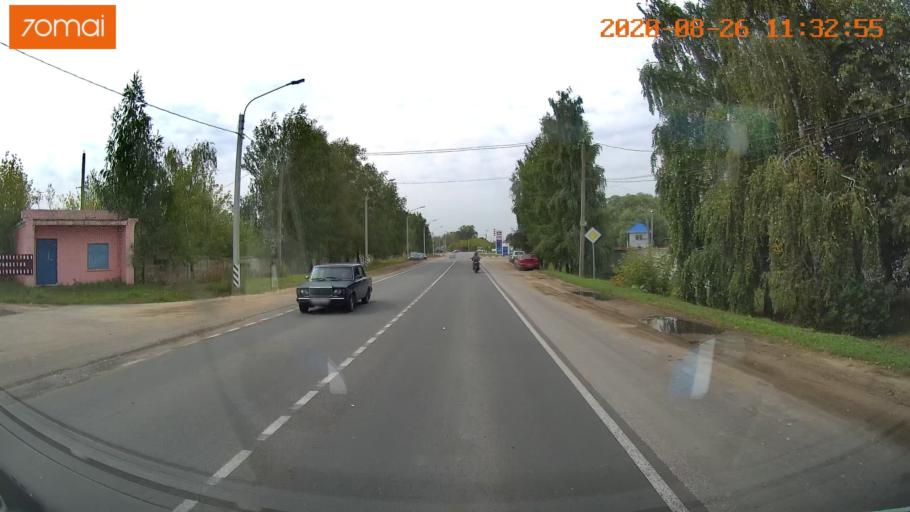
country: RU
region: Rjazan
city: Shilovo
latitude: 54.2994
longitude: 40.8598
